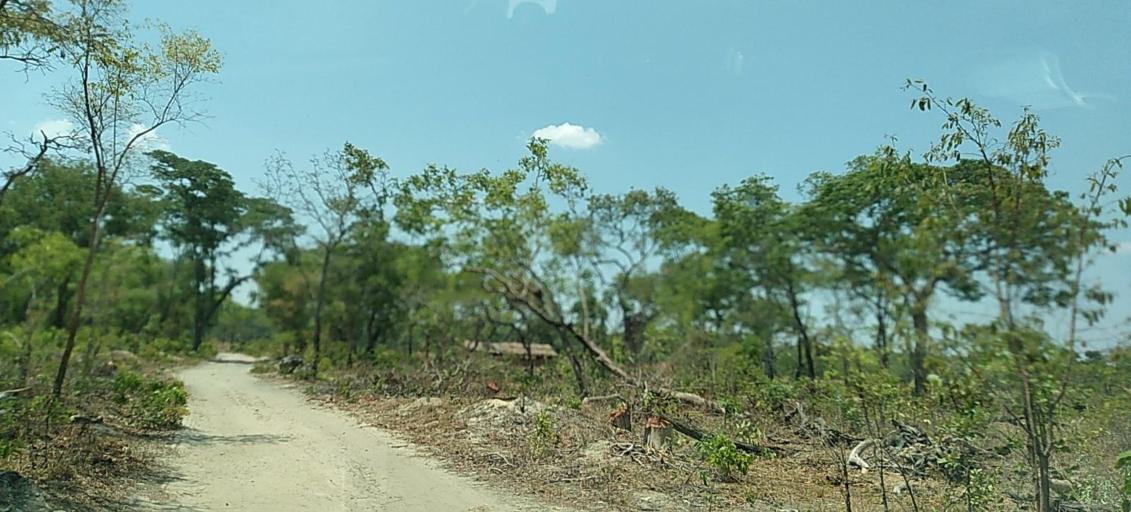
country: ZM
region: Copperbelt
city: Mpongwe
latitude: -13.6377
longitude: 28.4818
